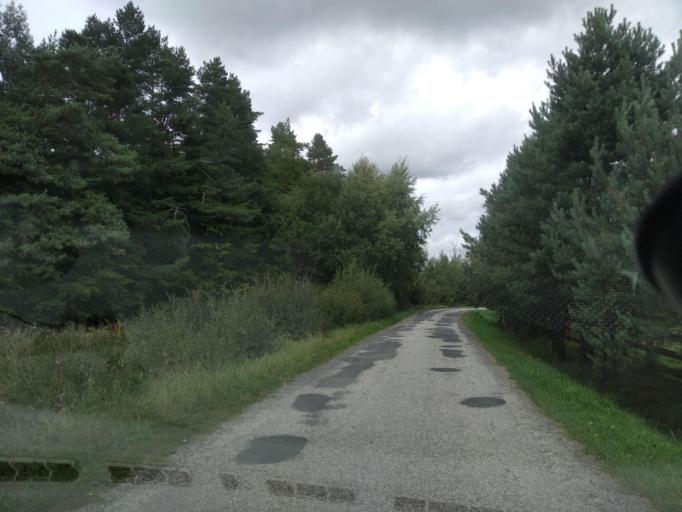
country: PL
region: Lesser Poland Voivodeship
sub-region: Powiat gorlicki
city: Uscie Gorlickie
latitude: 49.5405
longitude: 21.1796
